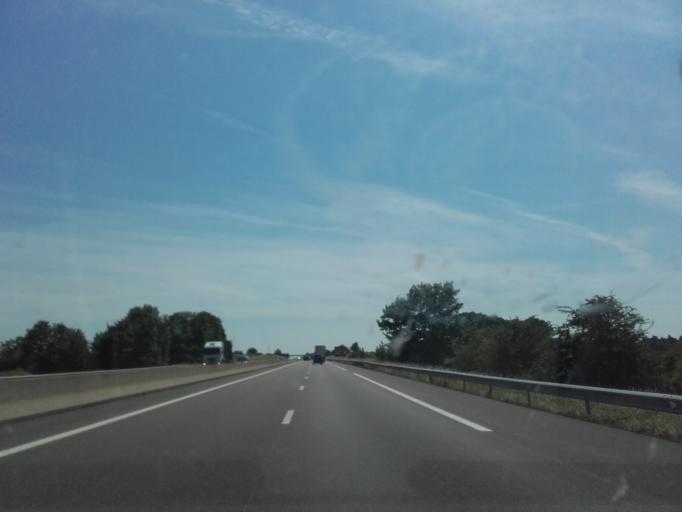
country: FR
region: Bourgogne
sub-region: Departement de la Cote-d'Or
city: Semur-en-Auxois
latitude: 47.4779
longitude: 4.1927
